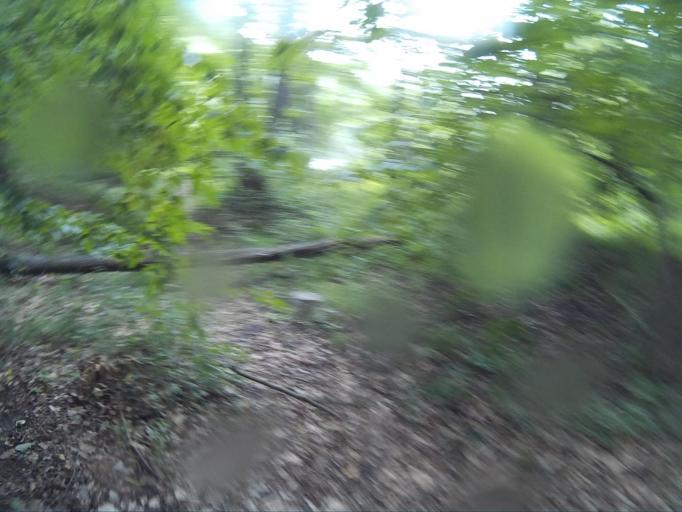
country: PL
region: Kujawsko-Pomorskie
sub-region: Powiat tucholski
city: Tuchola
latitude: 53.5837
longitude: 17.9085
